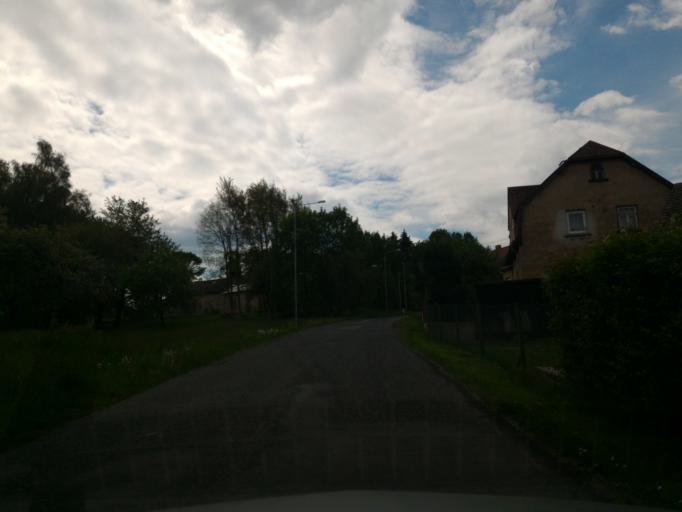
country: DE
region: Saxony
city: Neugersdorf
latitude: 50.9793
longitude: 14.5966
